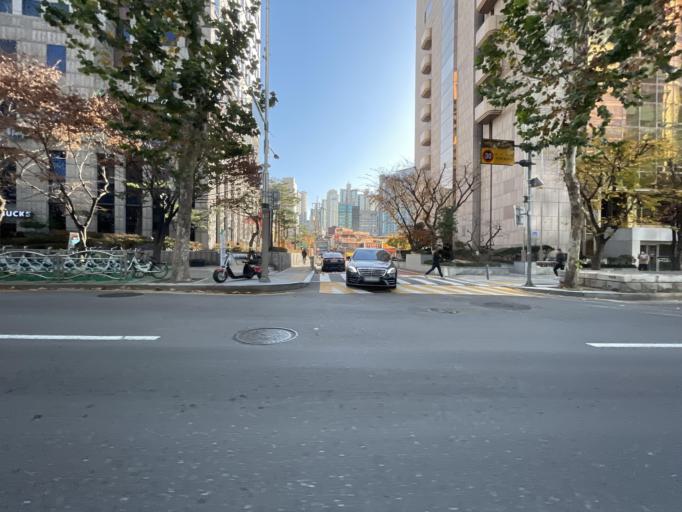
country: KR
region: Seoul
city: Seoul
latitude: 37.5459
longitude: 126.9525
